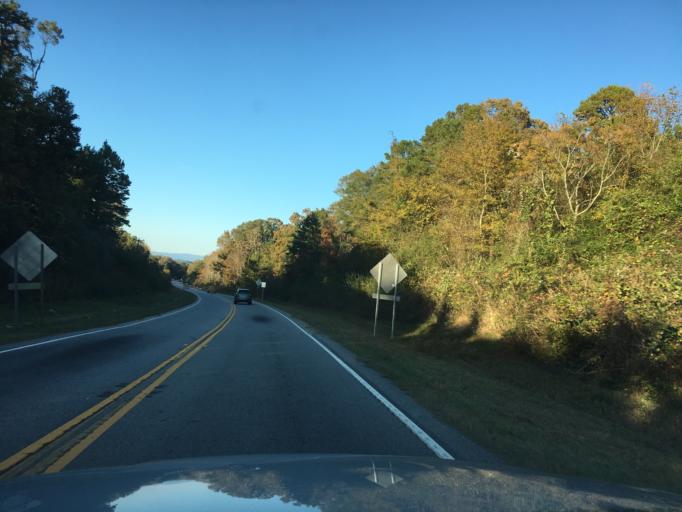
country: US
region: South Carolina
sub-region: Oconee County
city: Utica
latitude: 34.7139
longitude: -82.9233
